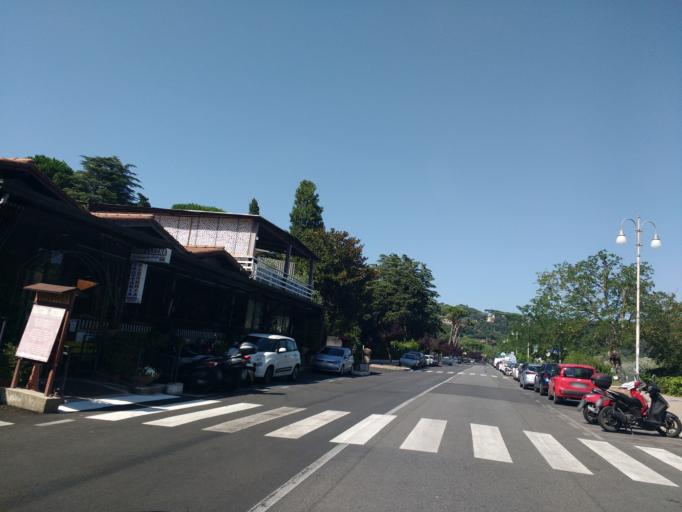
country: IT
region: Latium
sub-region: Citta metropolitana di Roma Capitale
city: Castel Gandolfo
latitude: 41.7558
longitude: 12.6514
